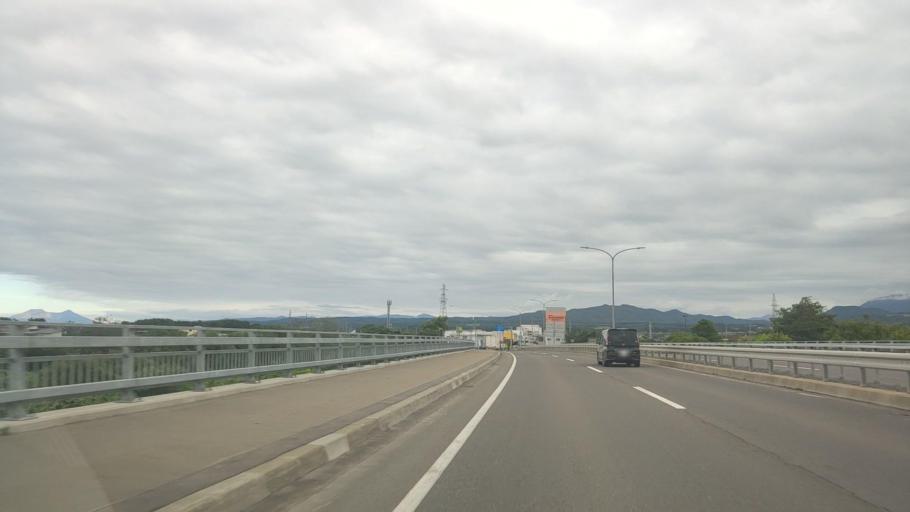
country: JP
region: Hokkaido
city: Nanae
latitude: 42.2637
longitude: 140.2734
